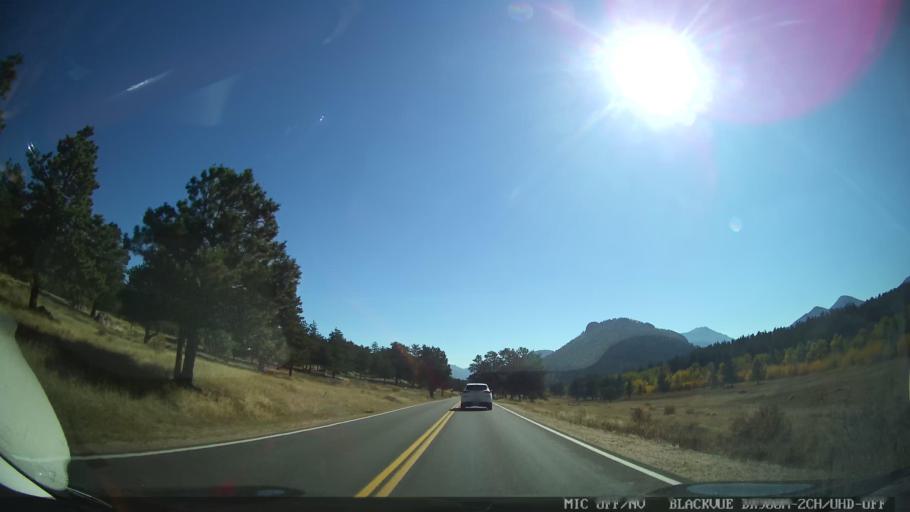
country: US
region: Colorado
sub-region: Larimer County
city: Estes Park
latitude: 40.3677
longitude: -105.5904
